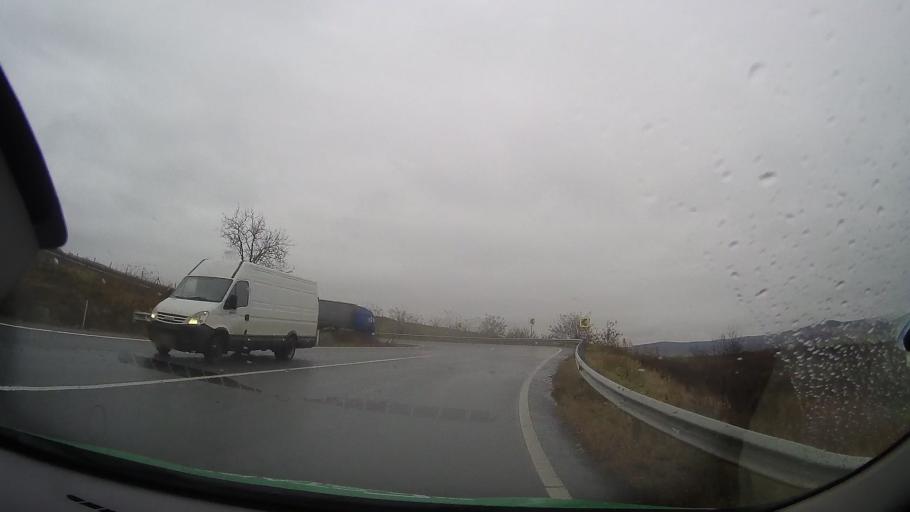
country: RO
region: Bistrita-Nasaud
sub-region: Comuna Teaca
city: Teaca
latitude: 46.9001
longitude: 24.5070
